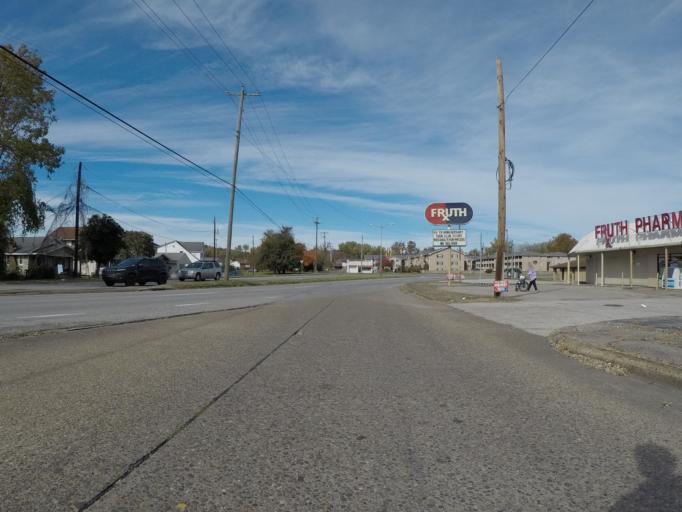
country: US
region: Ohio
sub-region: Lawrence County
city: Burlington
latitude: 38.4045
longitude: -82.5021
